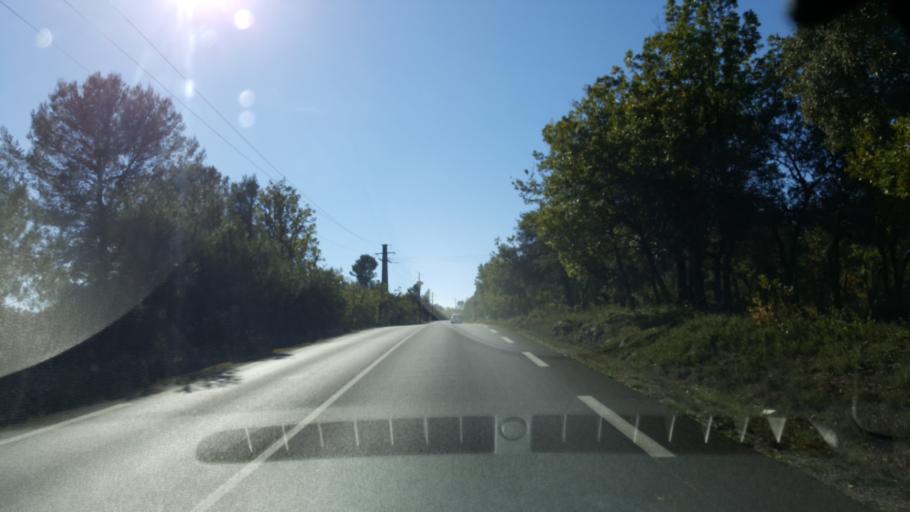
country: FR
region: Provence-Alpes-Cote d'Azur
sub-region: Departement du Var
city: Saint-Maximin-la-Sainte-Baume
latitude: 43.4274
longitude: 5.8462
